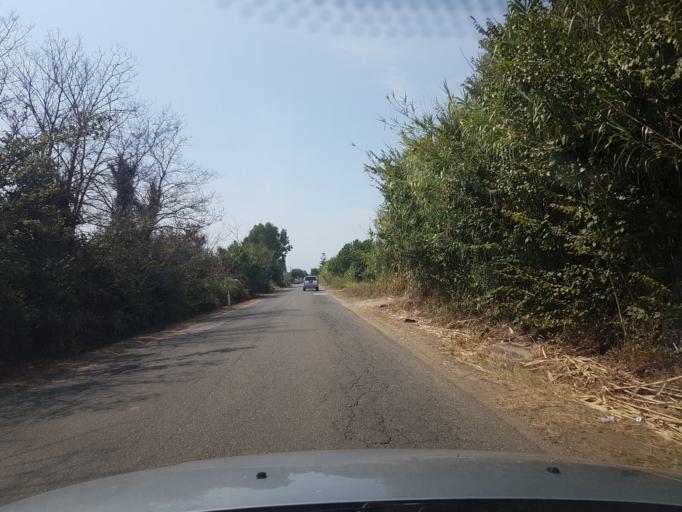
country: IT
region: Sardinia
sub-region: Provincia di Oristano
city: Solanas
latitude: 39.9219
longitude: 8.5441
